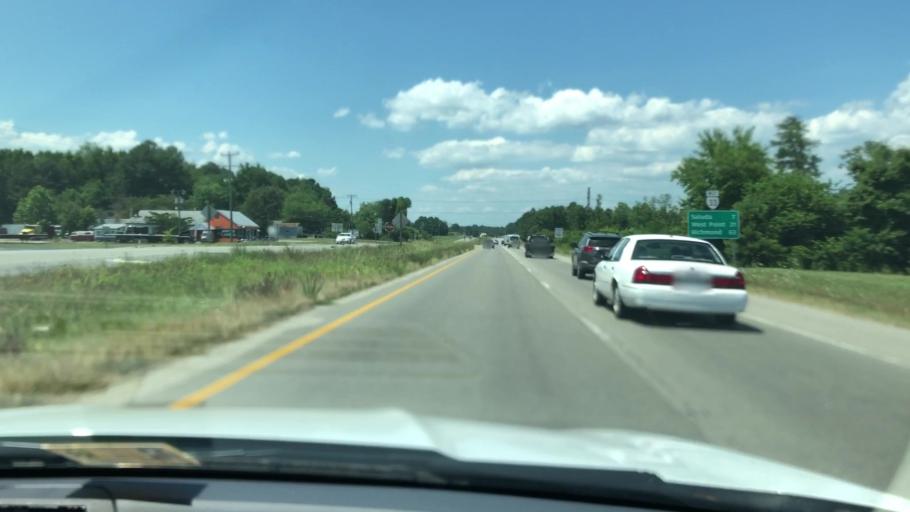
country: US
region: Virginia
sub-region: Middlesex County
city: Saluda
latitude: 37.5820
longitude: -76.4875
